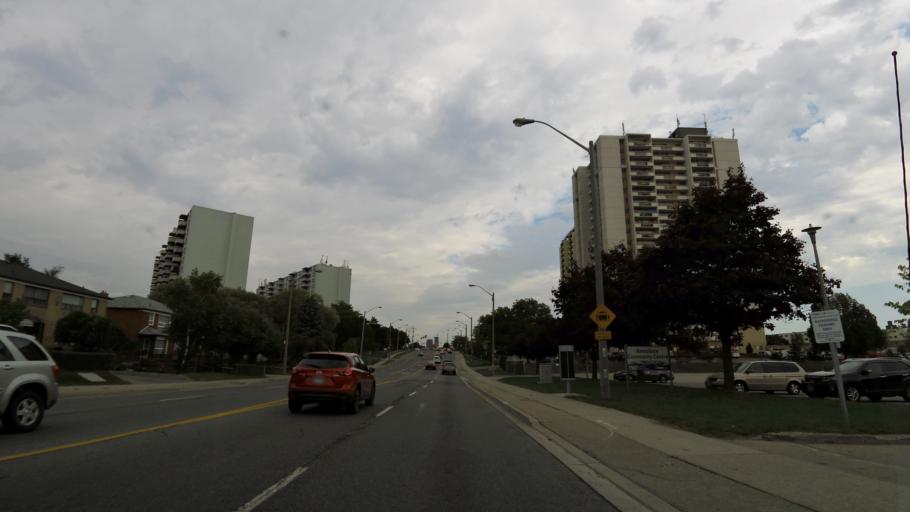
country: CA
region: Ontario
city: Toronto
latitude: 43.7075
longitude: -79.4821
